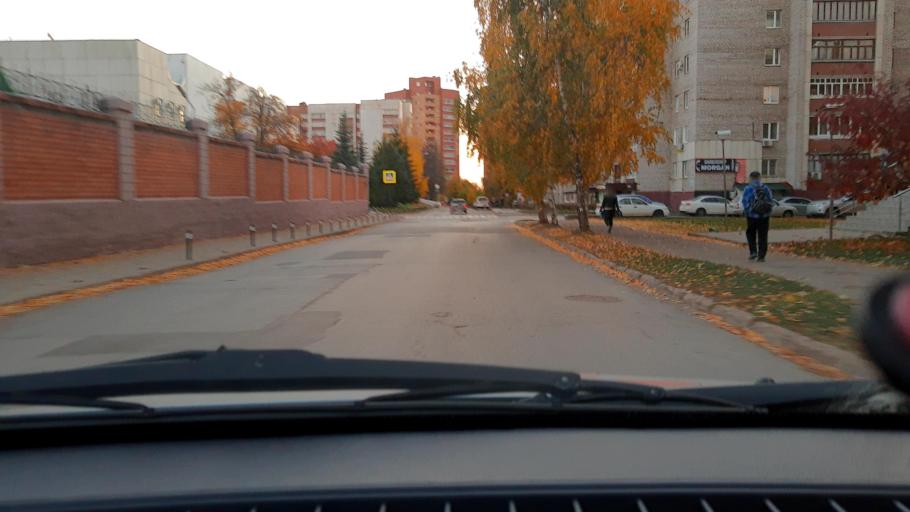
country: RU
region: Bashkortostan
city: Ufa
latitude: 54.6947
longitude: 55.9969
